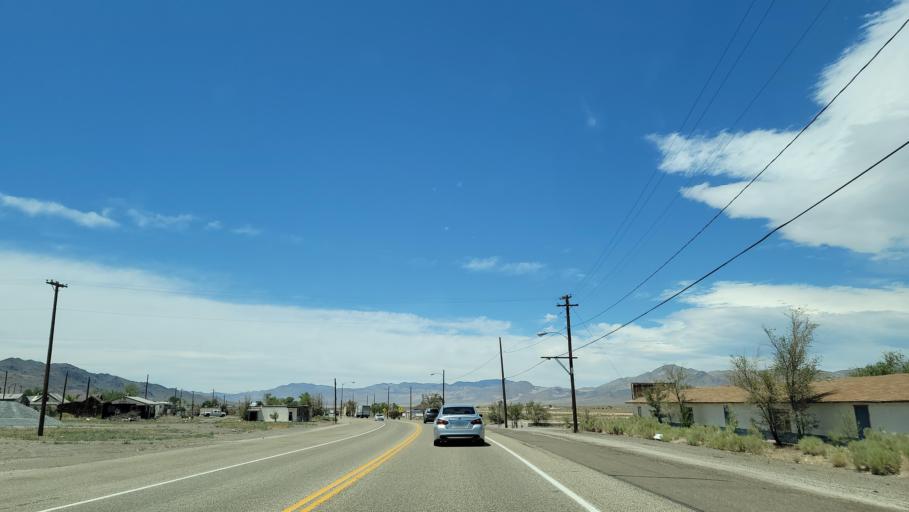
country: US
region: Nevada
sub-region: Mineral County
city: Hawthorne
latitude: 38.3877
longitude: -118.1072
